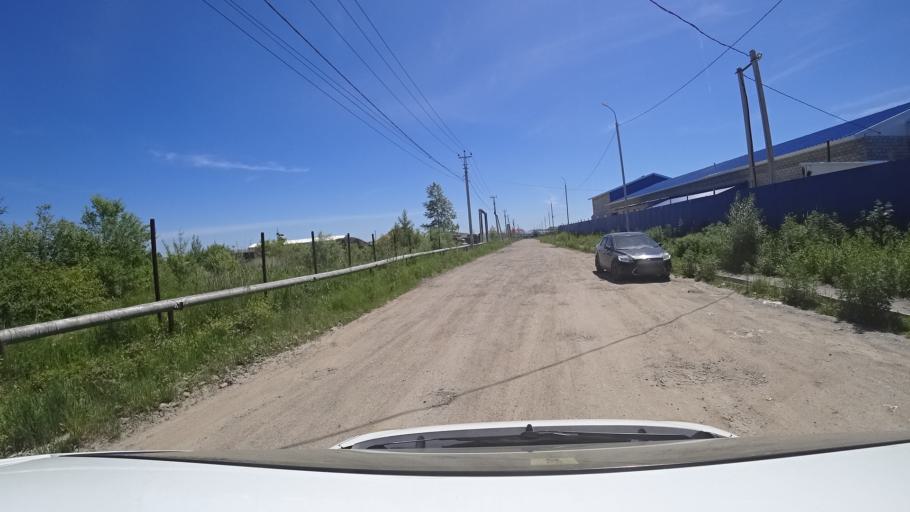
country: RU
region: Khabarovsk Krai
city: Topolevo
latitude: 48.5046
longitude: 135.1811
